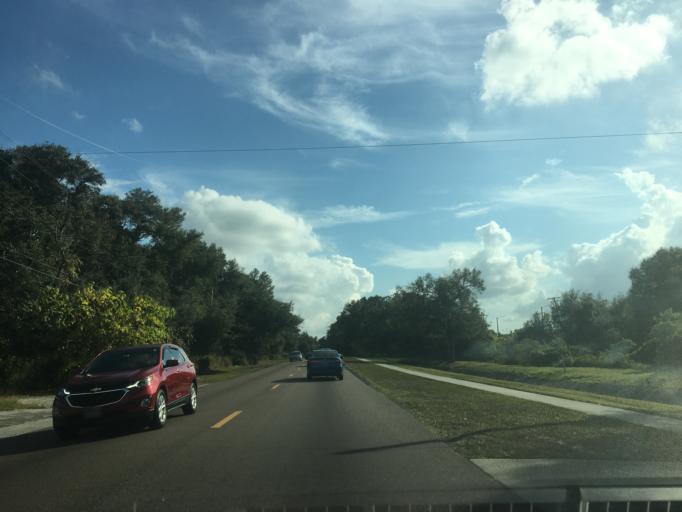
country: US
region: Florida
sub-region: Hillsborough County
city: Temple Terrace
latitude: 28.0145
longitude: -82.4313
